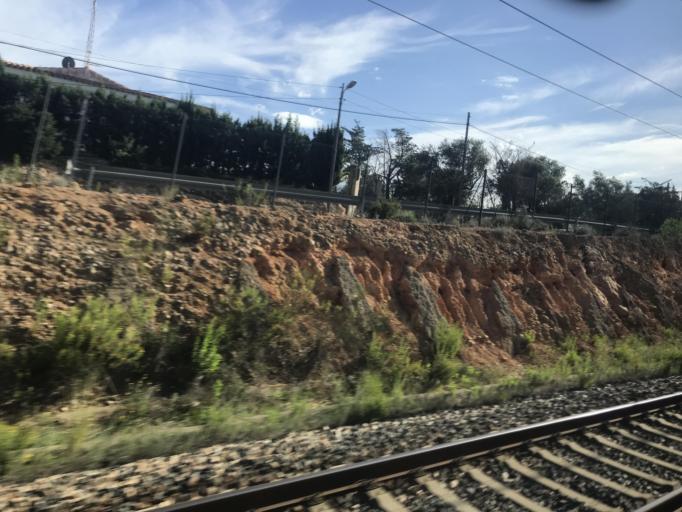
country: ES
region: Catalonia
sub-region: Provincia de Tarragona
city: L'Ampolla
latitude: 40.8268
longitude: 0.7328
